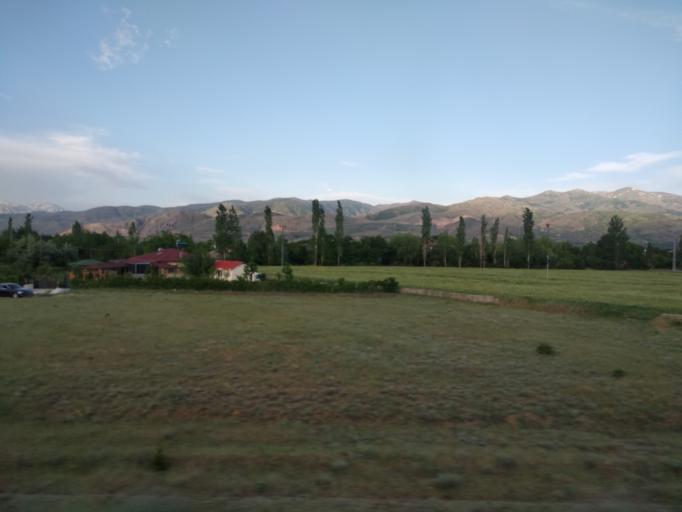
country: TR
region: Erzincan
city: Catalarmut
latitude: 39.8058
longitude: 39.3675
